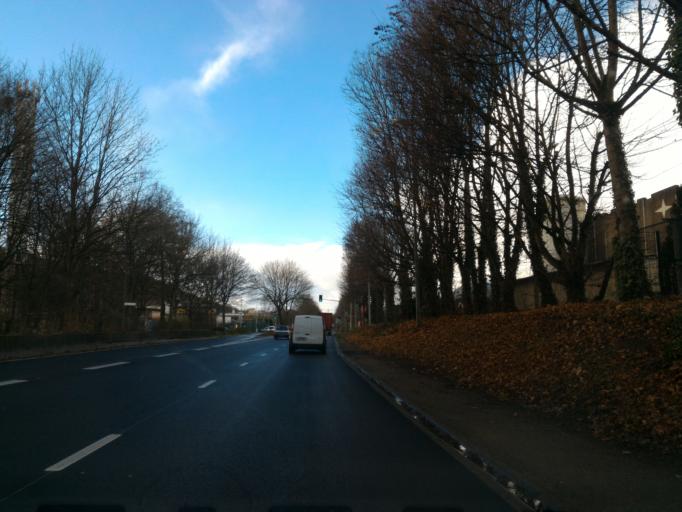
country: FR
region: Haute-Normandie
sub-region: Departement de la Seine-Maritime
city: Darnetal
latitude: 49.4365
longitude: 1.1355
